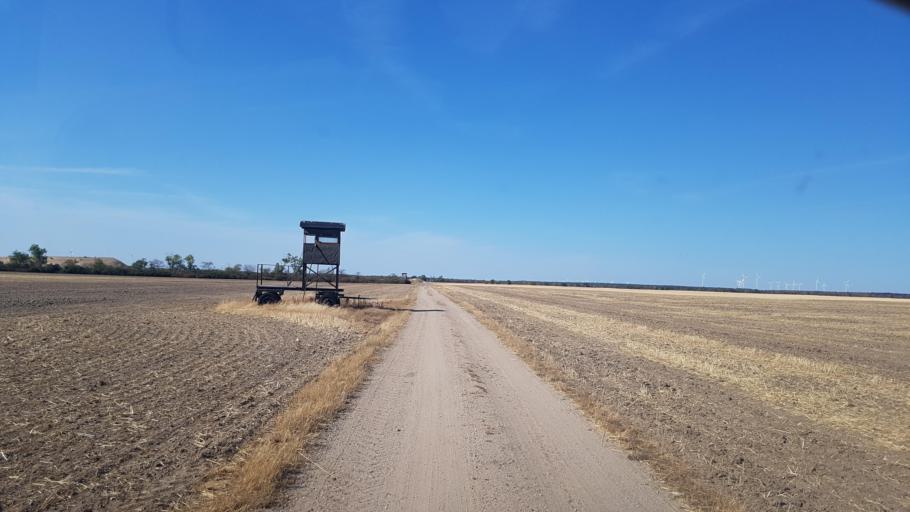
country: DE
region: Brandenburg
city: Muhlberg
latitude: 51.4124
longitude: 13.2866
